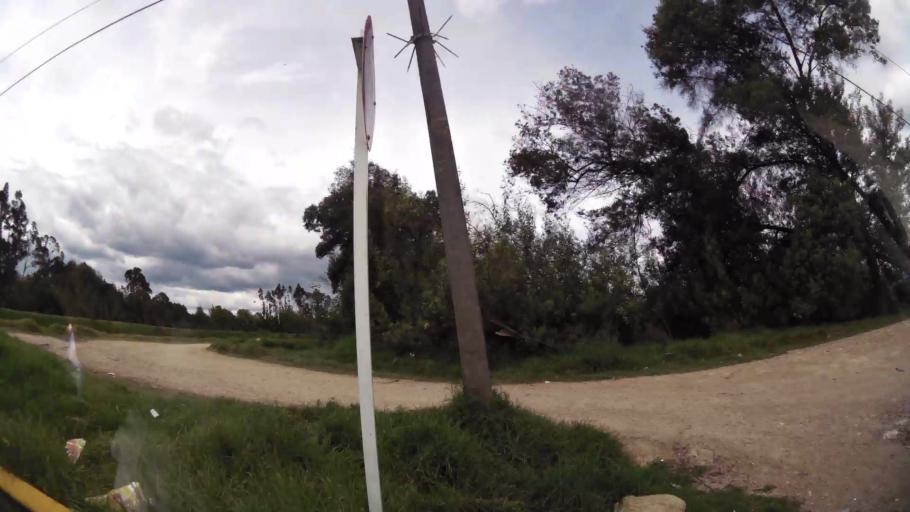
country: CO
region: Cundinamarca
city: Funza
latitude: 4.7256
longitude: -74.1486
